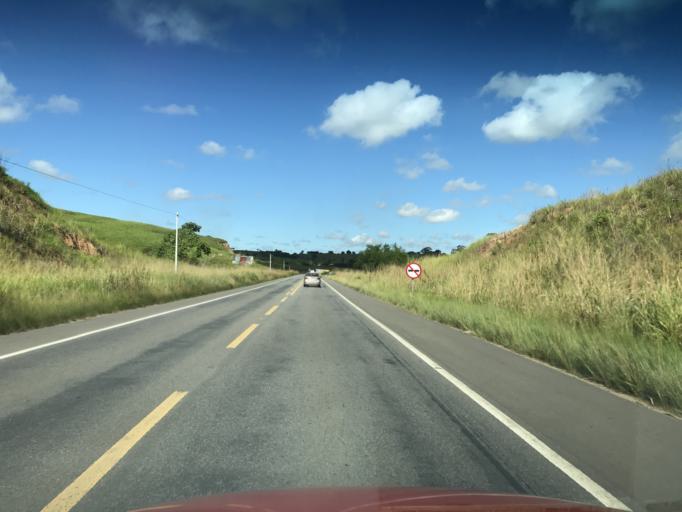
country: BR
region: Bahia
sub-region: Conceicao Do Almeida
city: Muritiba
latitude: -12.9283
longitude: -39.2524
